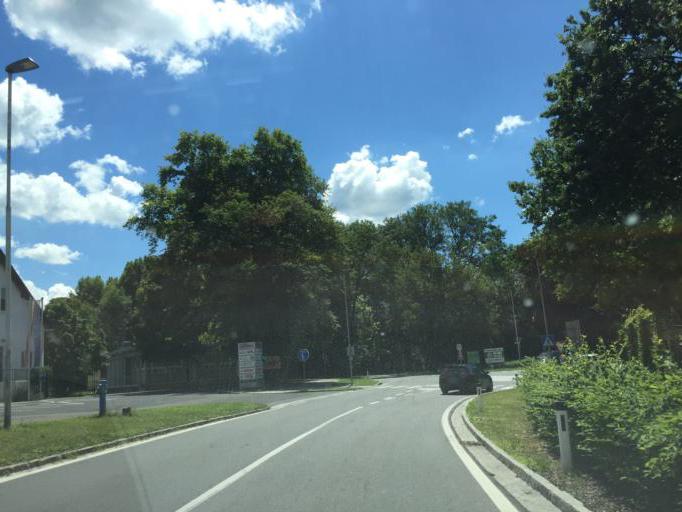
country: AT
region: Styria
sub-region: Politischer Bezirk Suedoststeiermark
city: Bad Radkersburg
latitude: 46.6871
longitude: 15.9916
